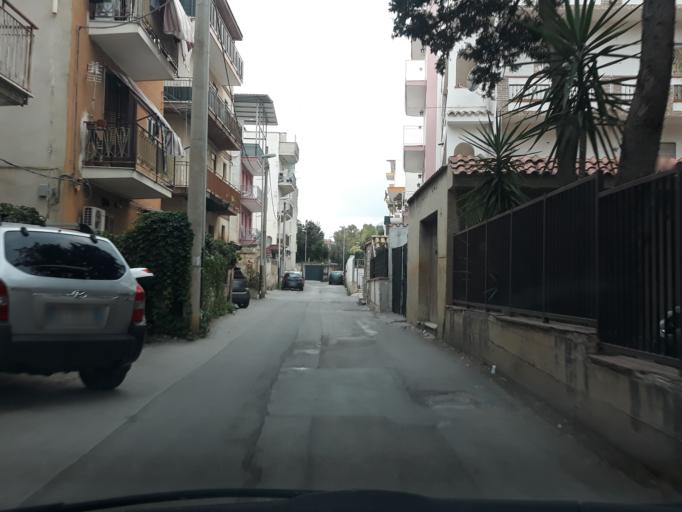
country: IT
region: Sicily
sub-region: Palermo
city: Monreale
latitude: 38.0935
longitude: 13.3182
